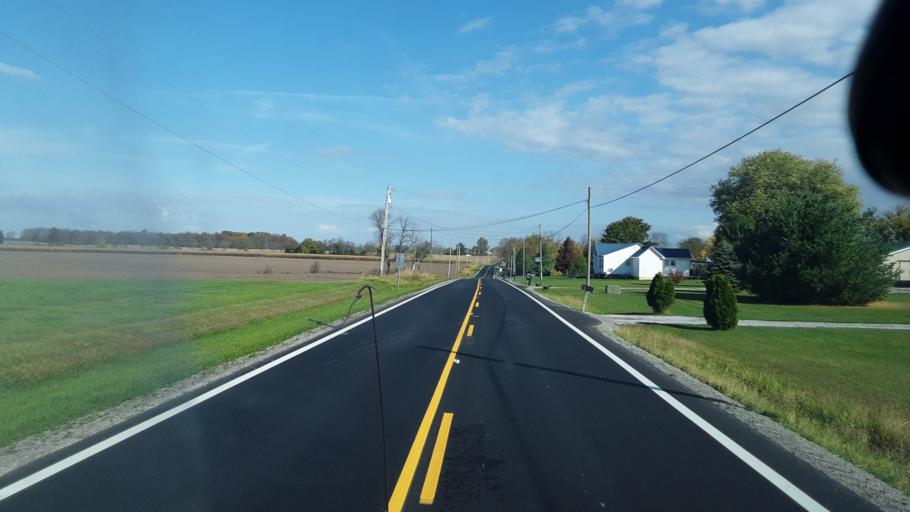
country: US
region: Ohio
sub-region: Highland County
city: Leesburg
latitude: 39.2922
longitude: -83.5908
